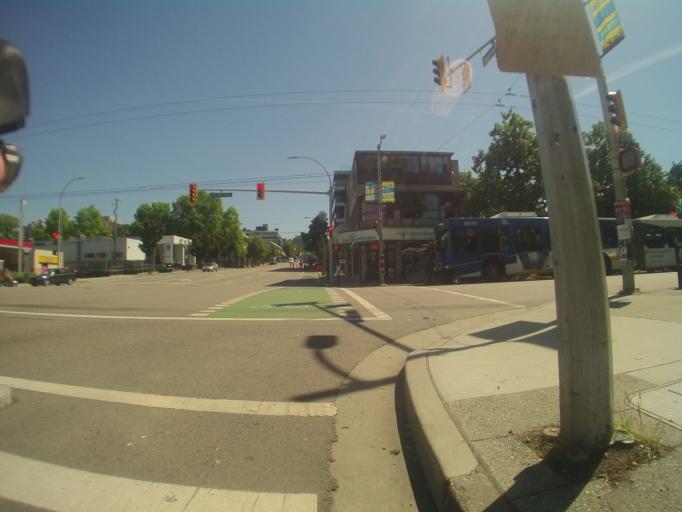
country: CA
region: British Columbia
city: West End
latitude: 49.2682
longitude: -123.1458
